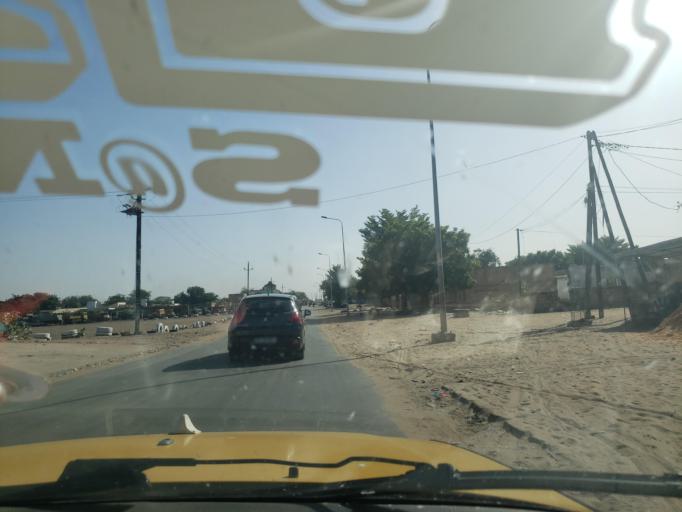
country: SN
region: Louga
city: Louga
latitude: 15.6215
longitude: -16.2104
